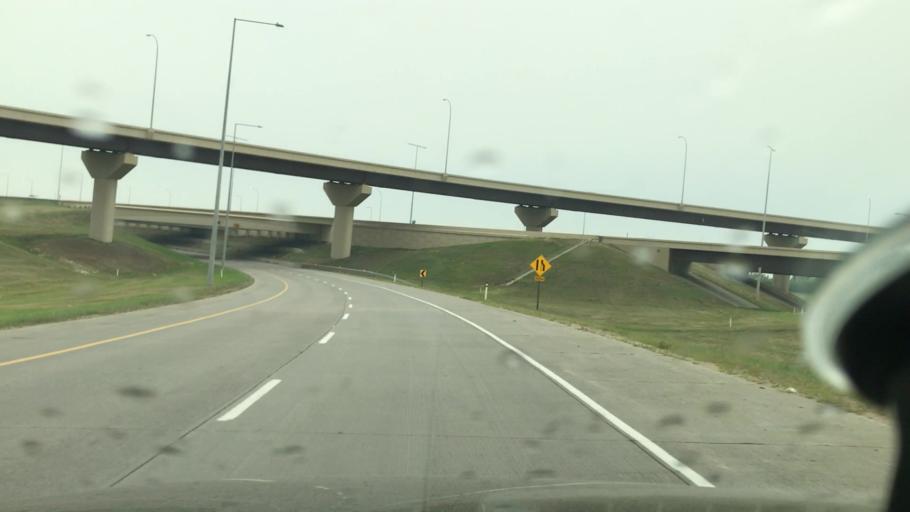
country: CA
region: Alberta
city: Beaumont
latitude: 53.4357
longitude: -113.4935
